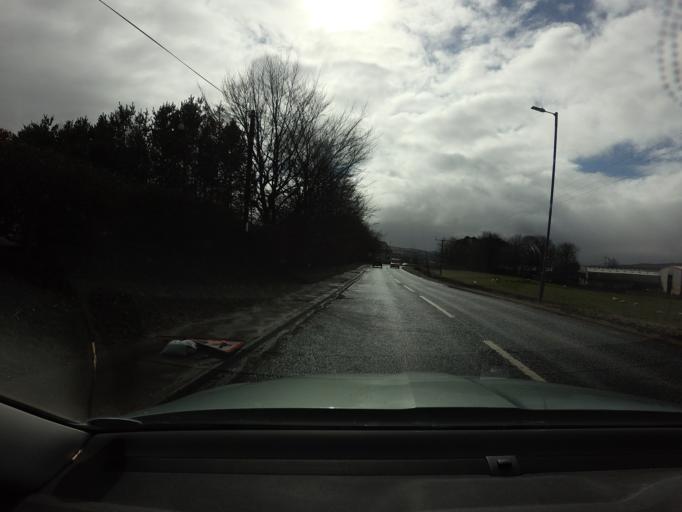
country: GB
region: Scotland
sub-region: South Lanarkshire
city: Douglas
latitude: 55.5924
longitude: -3.7933
